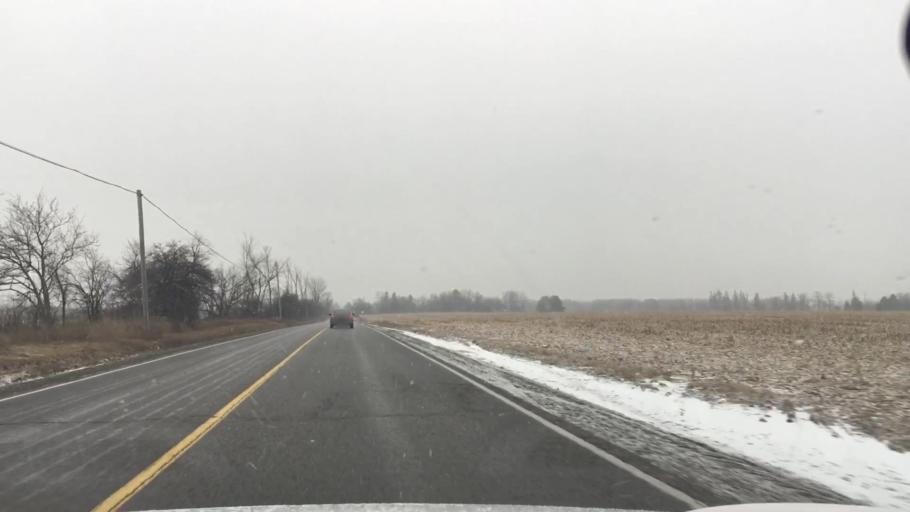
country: CA
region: Ontario
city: Pickering
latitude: 43.8795
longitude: -79.1807
